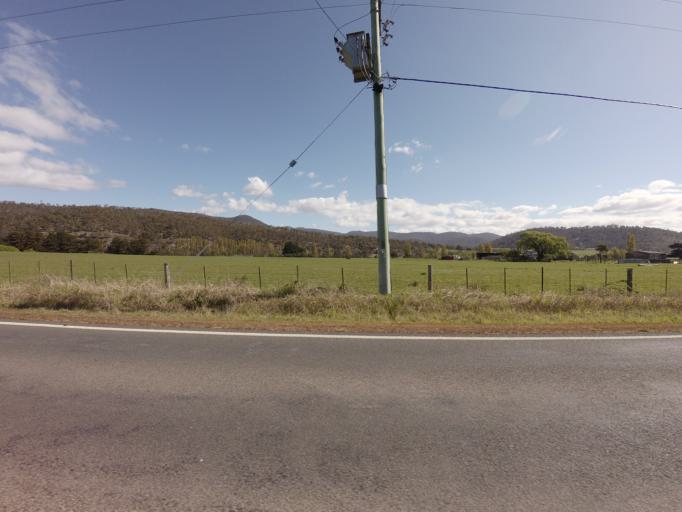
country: AU
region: Tasmania
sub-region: Derwent Valley
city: New Norfolk
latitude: -42.7741
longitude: 147.0353
